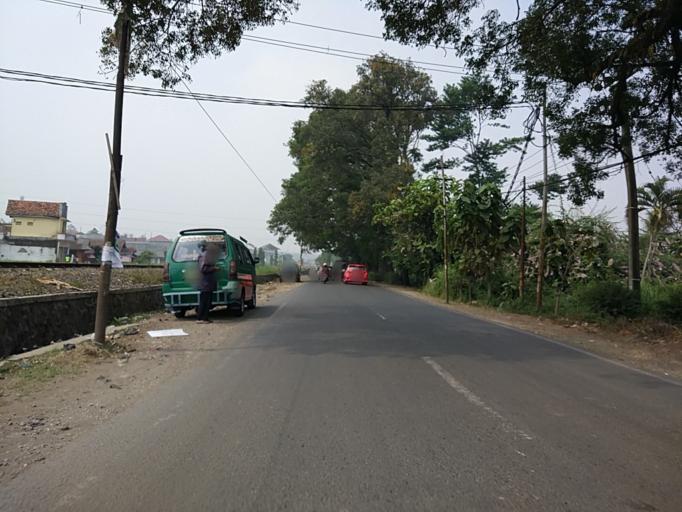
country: ID
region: West Java
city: Padalarang
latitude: -6.8386
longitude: 107.4926
